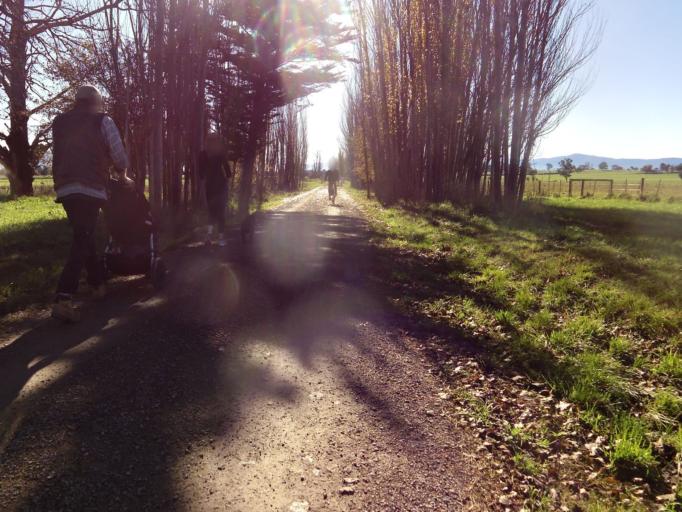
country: AU
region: Victoria
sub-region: Yarra Ranges
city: Lilydale
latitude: -37.7116
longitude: 145.3682
